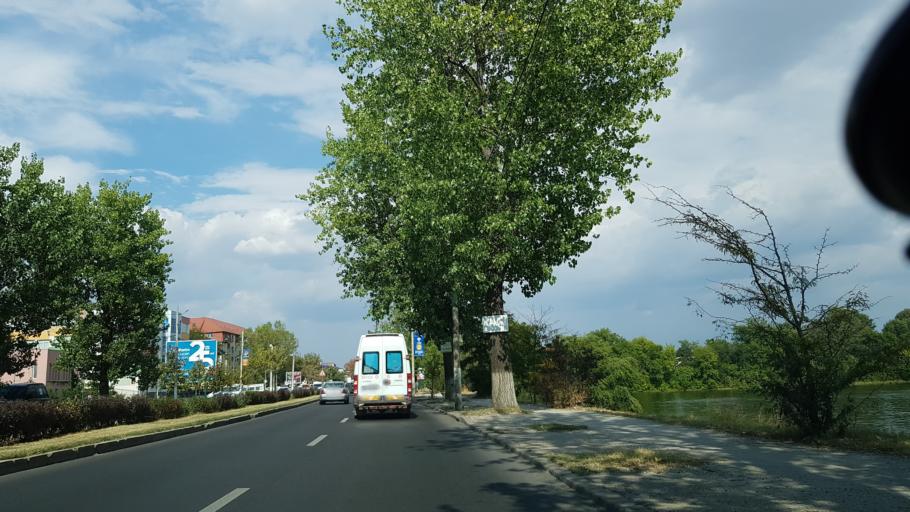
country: RO
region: Ilfov
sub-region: Comuna Pantelimon
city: Pantelimon
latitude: 44.4439
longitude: 26.2003
